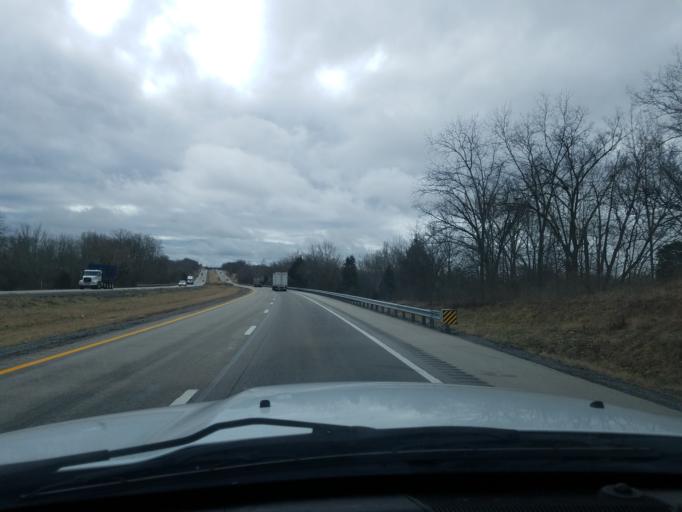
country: US
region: Kentucky
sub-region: Montgomery County
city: Mount Sterling
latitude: 38.0473
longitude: -84.0658
